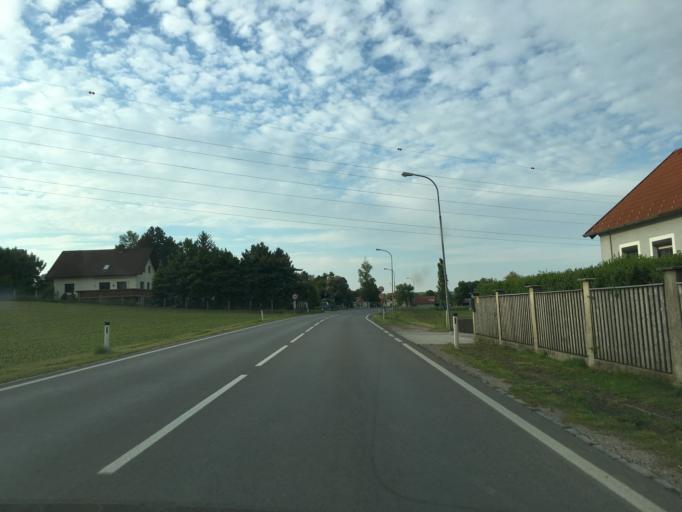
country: AT
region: Lower Austria
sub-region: Politischer Bezirk Sankt Polten
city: Neulengbach
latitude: 48.2121
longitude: 15.9117
